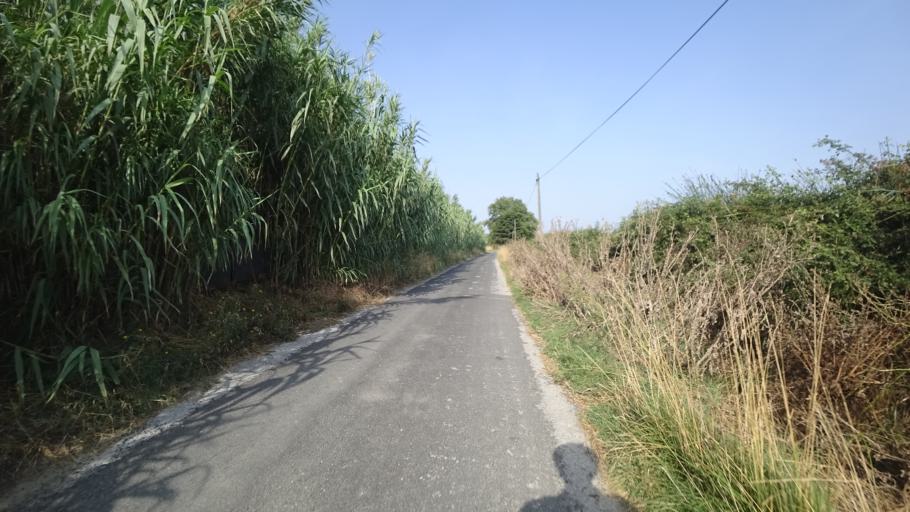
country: FR
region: Languedoc-Roussillon
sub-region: Departement des Pyrenees-Orientales
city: Villelongue-de-la-Salanque
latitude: 42.7351
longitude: 2.9933
